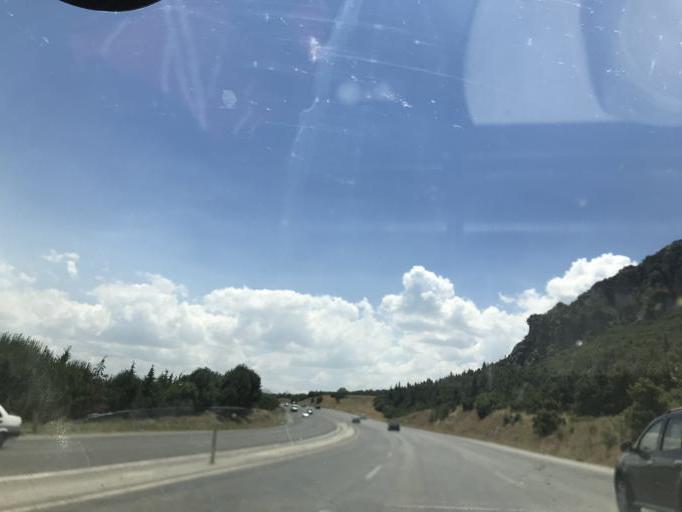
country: TR
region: Denizli
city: Honaz
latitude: 37.7120
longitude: 29.2052
